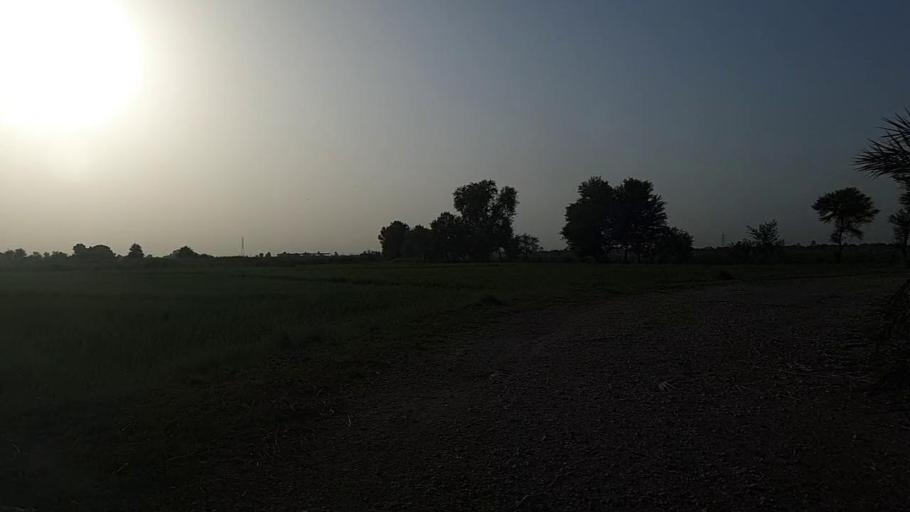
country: PK
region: Sindh
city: Naushahro Firoz
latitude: 26.8063
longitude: 68.1118
